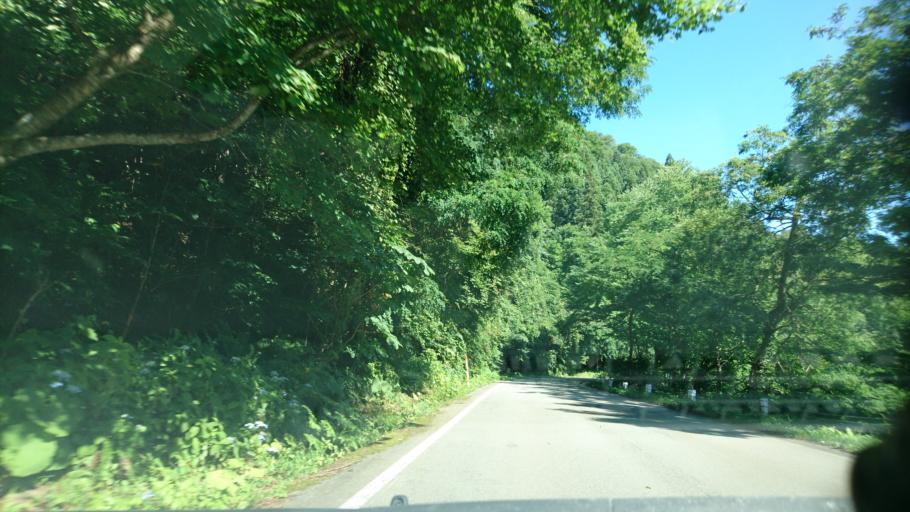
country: JP
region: Akita
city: Kakunodatemachi
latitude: 39.7308
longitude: 140.6318
